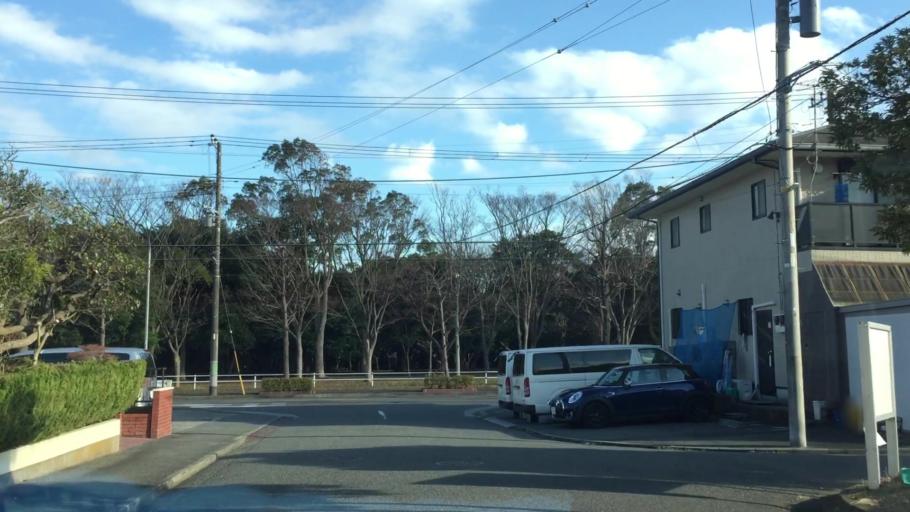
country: JP
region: Kanagawa
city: Zushi
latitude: 35.3385
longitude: 139.5950
